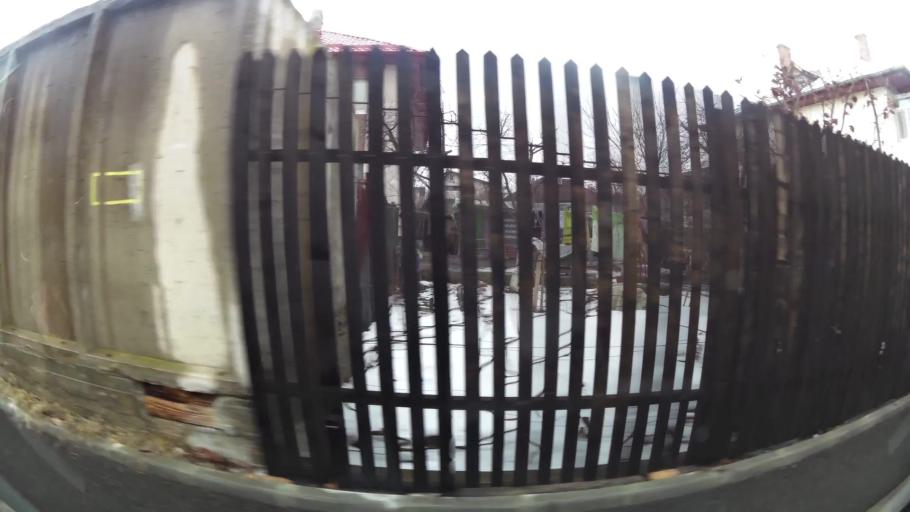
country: RO
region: Ilfov
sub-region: Comuna Otopeni
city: Otopeni
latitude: 44.5527
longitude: 26.0742
